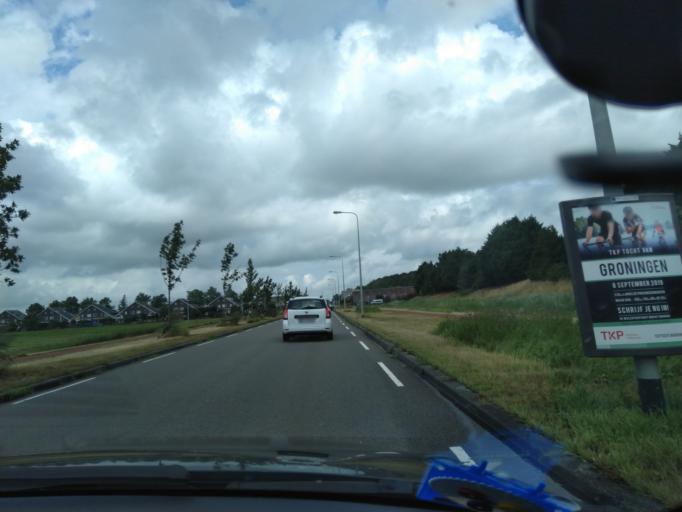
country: NL
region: Groningen
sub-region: Gemeente Groningen
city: Groningen
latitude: 53.2198
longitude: 6.5133
